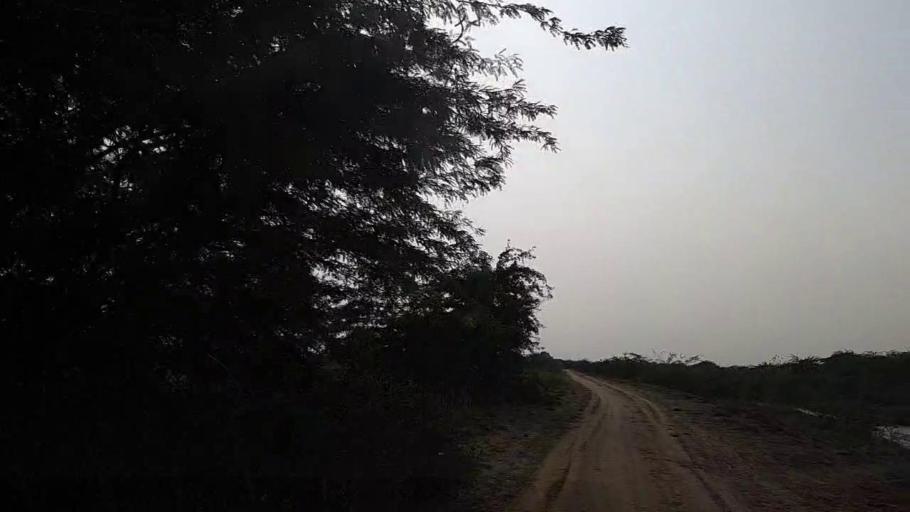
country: PK
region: Sindh
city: Gharo
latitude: 24.6606
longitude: 67.6266
